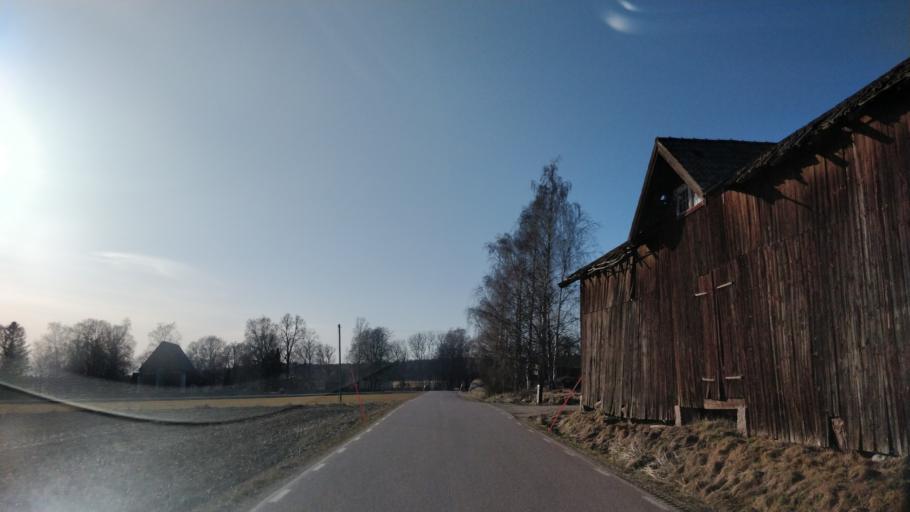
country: SE
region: Uppsala
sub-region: Enkopings Kommun
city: Orsundsbro
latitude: 59.7511
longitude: 17.1773
